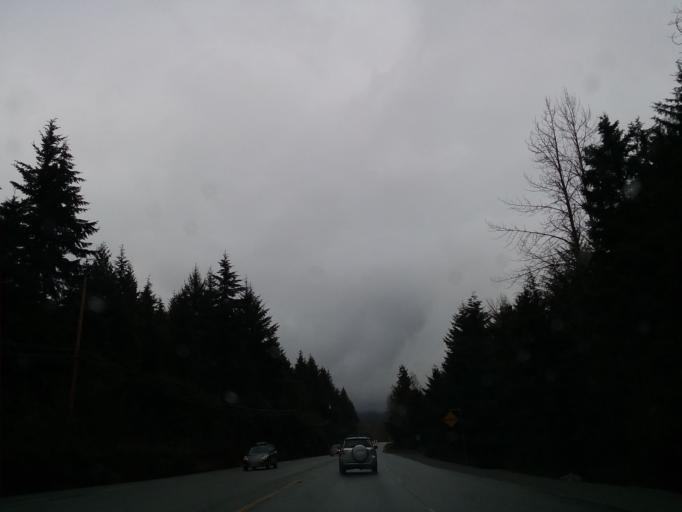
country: CA
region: British Columbia
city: Whistler
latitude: 50.1226
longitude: -122.9597
